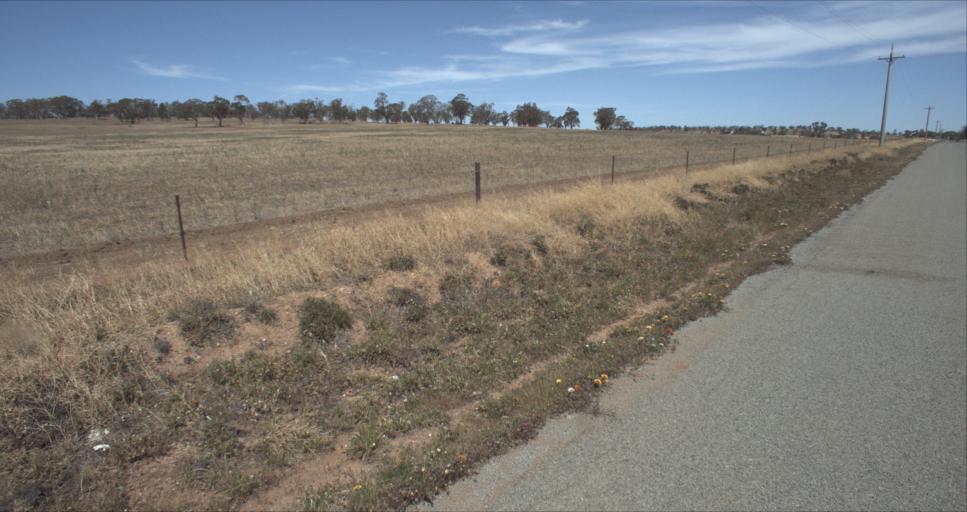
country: AU
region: New South Wales
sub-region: Leeton
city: Leeton
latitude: -34.6086
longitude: 146.4350
